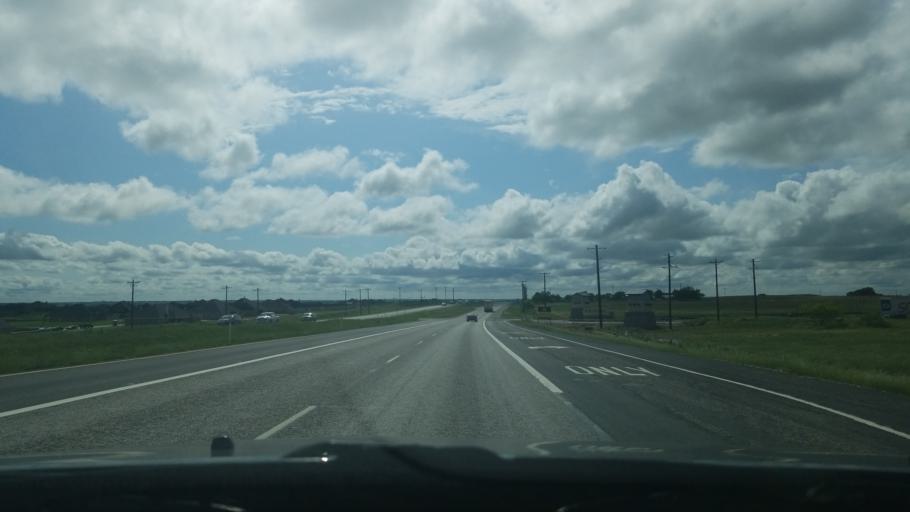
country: US
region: Texas
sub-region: Denton County
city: Ponder
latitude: 33.2416
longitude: -97.3606
